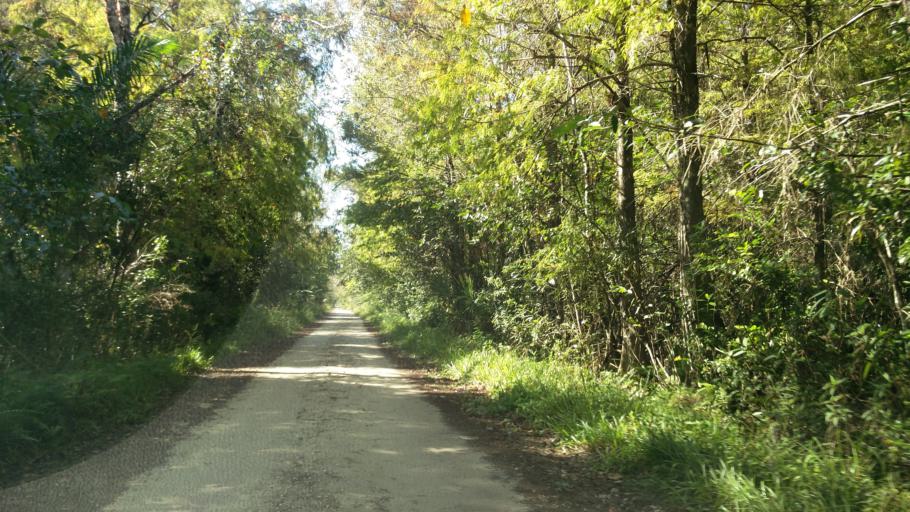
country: US
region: Florida
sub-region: Collier County
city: Lely Resort
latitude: 25.9799
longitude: -81.3990
